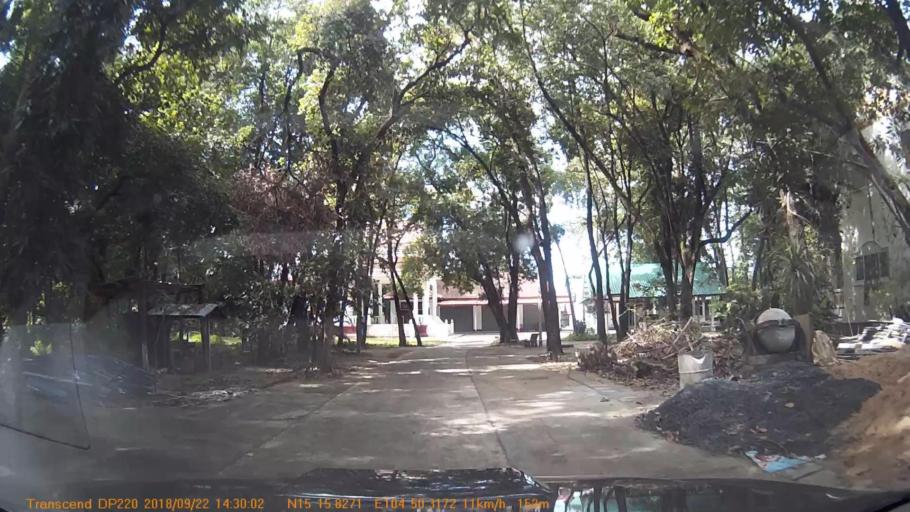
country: TH
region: Changwat Ubon Ratchathani
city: Ubon Ratchathani
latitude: 15.2638
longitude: 104.8386
